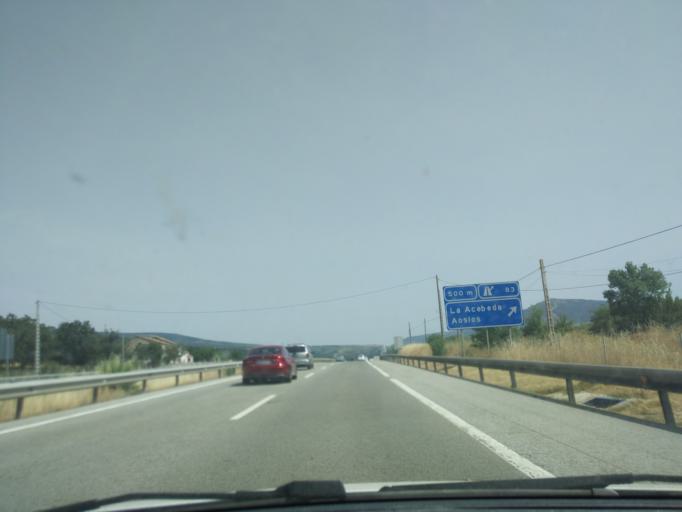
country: ES
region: Madrid
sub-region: Provincia de Madrid
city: Braojos
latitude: 41.0529
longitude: -3.6146
